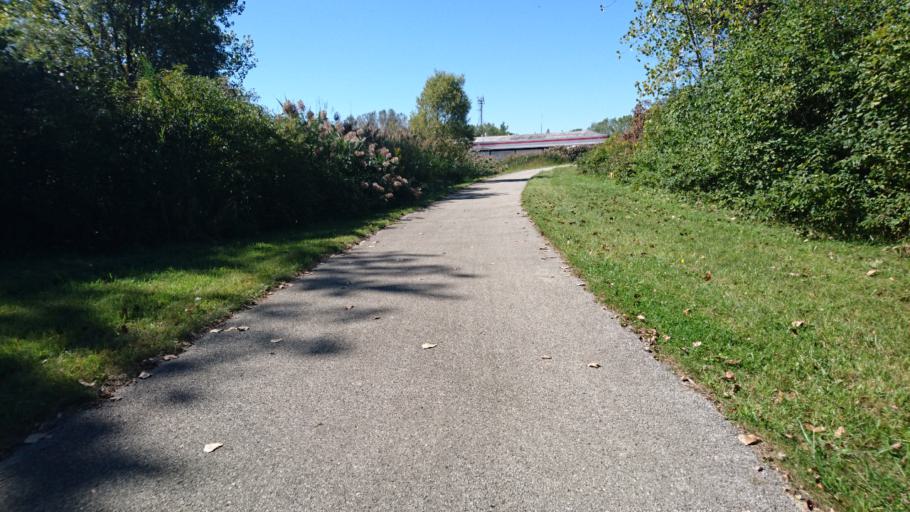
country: US
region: Illinois
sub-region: Cook County
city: Lansing
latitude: 41.5822
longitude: -87.5494
